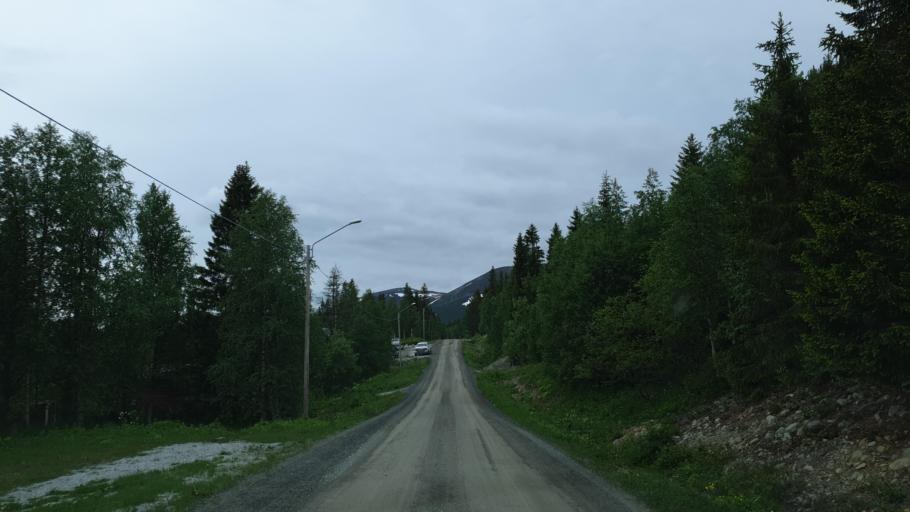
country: SE
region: Vaesterbotten
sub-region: Vilhelmina Kommun
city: Sjoberg
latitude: 65.3481
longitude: 15.8568
